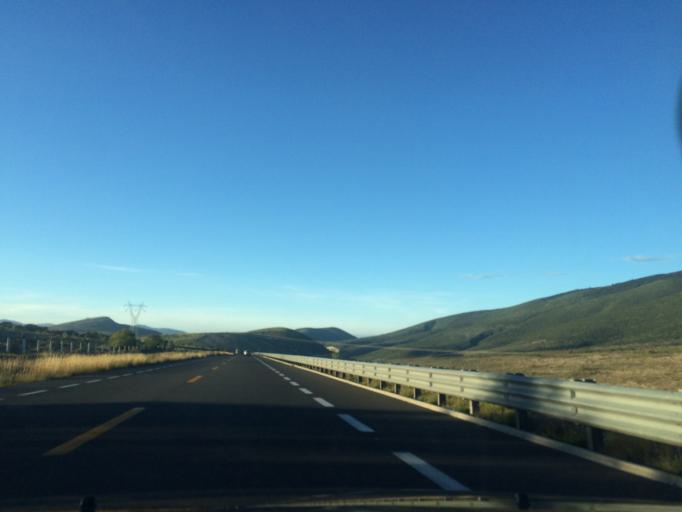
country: MX
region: Puebla
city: Morelos Canada
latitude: 18.6975
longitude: -97.4645
